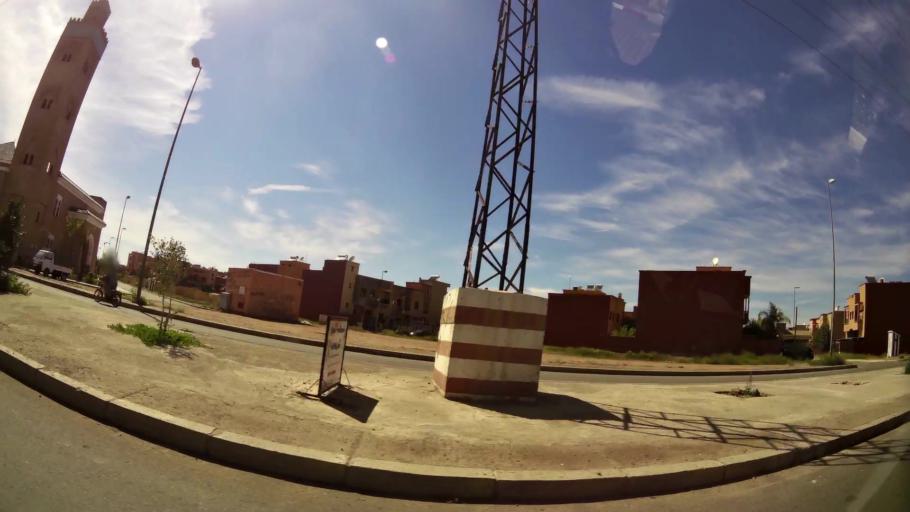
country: MA
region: Marrakech-Tensift-Al Haouz
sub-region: Marrakech
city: Marrakesh
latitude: 31.6404
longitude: -8.0425
